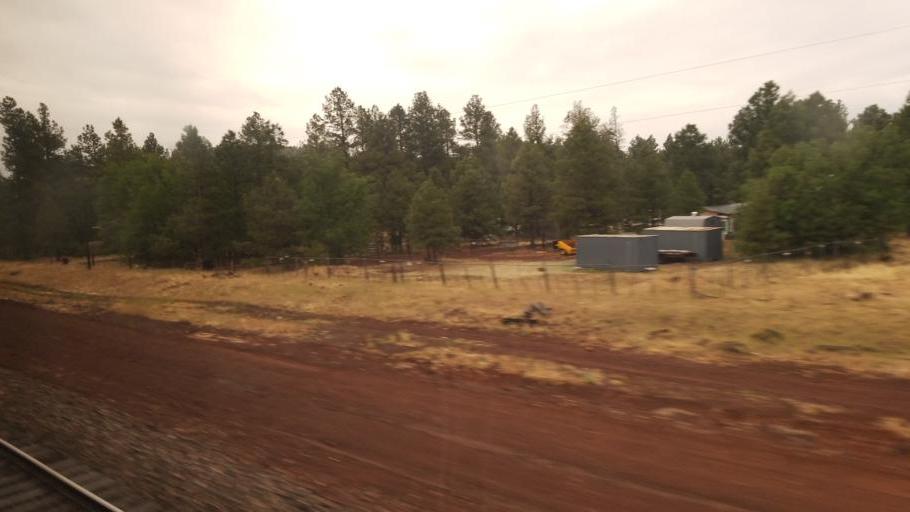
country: US
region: Arizona
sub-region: Coconino County
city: Parks
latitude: 35.2531
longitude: -111.9374
